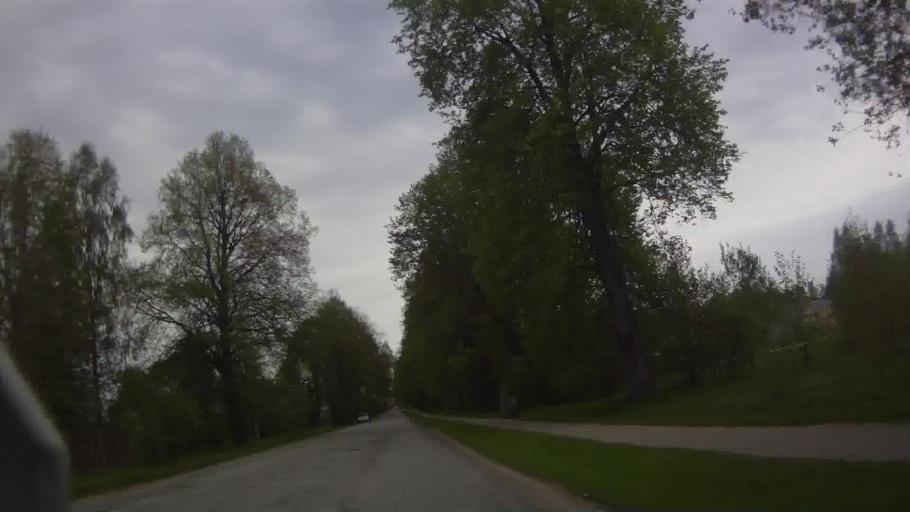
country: LV
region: Incukalns
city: Incukalns
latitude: 57.1037
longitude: 24.6832
